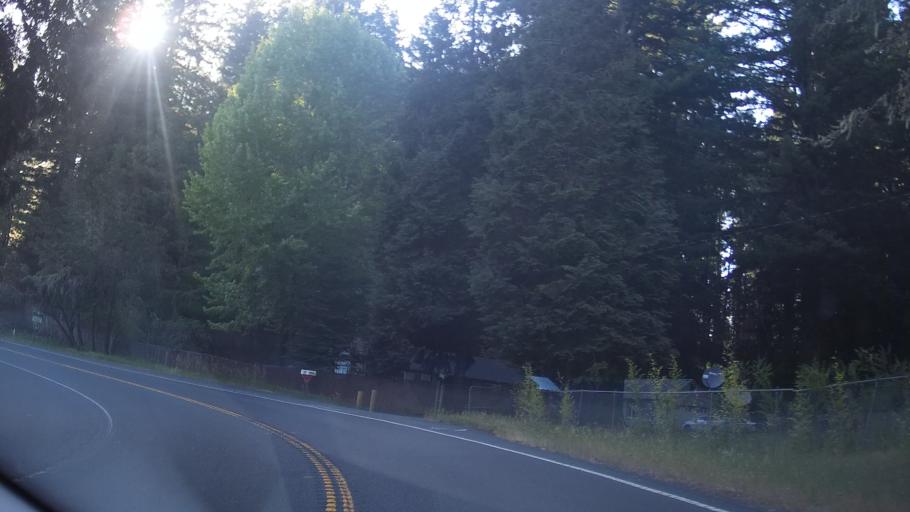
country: US
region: California
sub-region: Mendocino County
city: Fort Bragg
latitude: 39.3635
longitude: -123.6649
